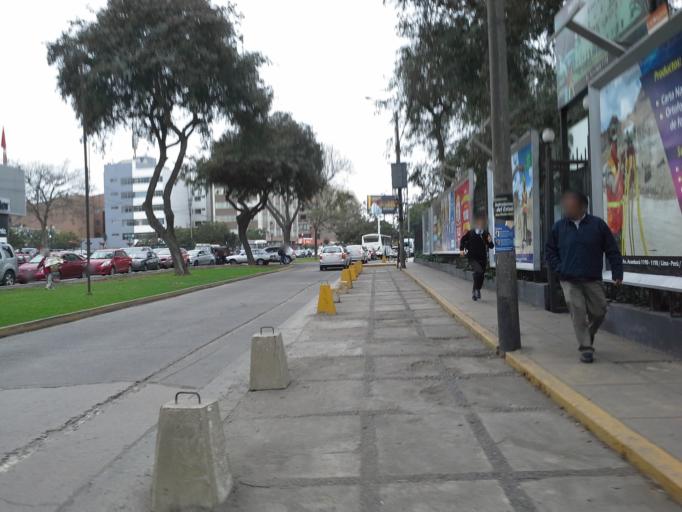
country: PE
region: Lima
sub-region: Lima
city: San Luis
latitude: -12.1023
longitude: -77.0171
